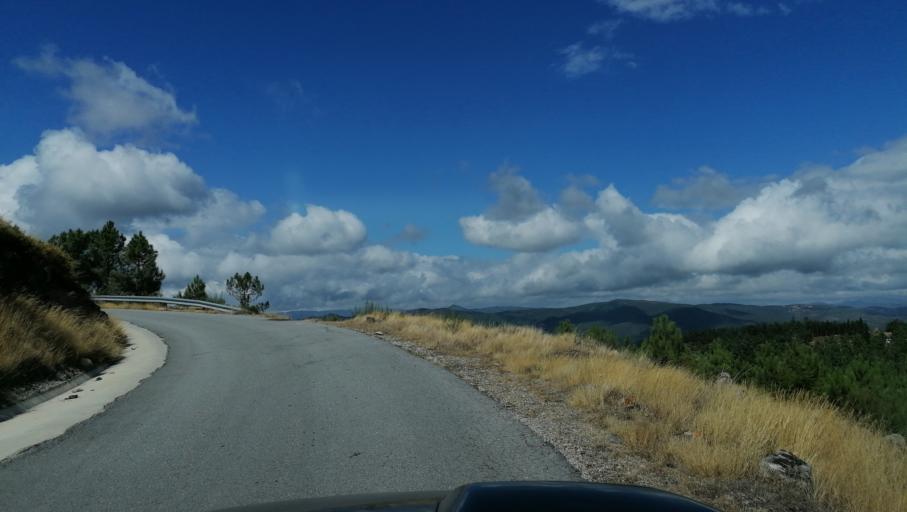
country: PT
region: Vila Real
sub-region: Vila Pouca de Aguiar
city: Vila Pouca de Aguiar
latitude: 41.5612
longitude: -7.6639
